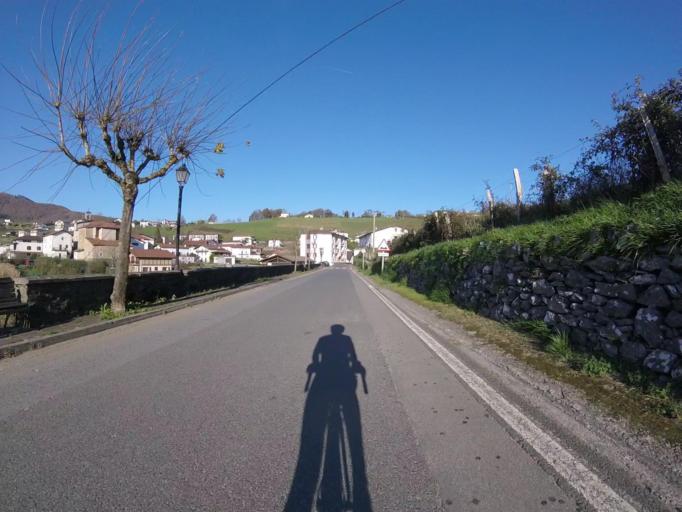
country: ES
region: Navarre
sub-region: Provincia de Navarra
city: Igantzi
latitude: 43.2245
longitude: -1.6983
